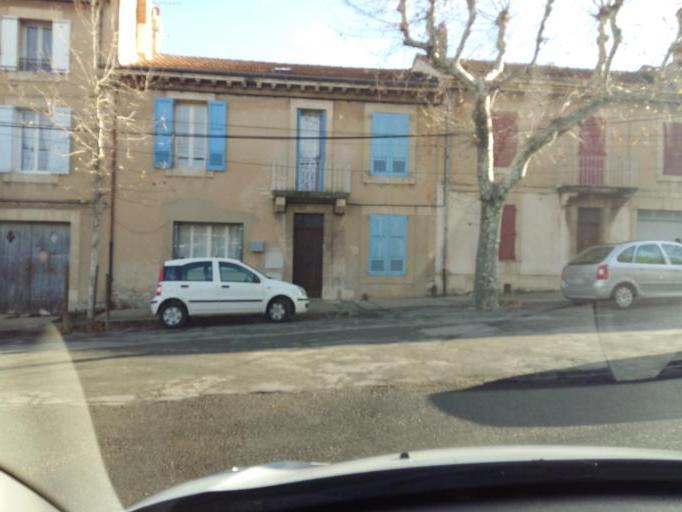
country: FR
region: Provence-Alpes-Cote d'Azur
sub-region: Departement du Vaucluse
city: Apt
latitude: 43.8731
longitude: 5.3998
